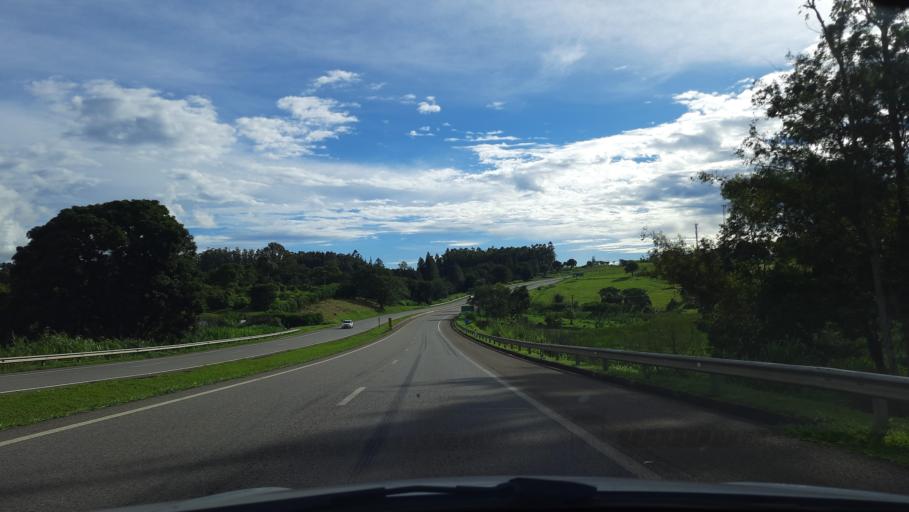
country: BR
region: Sao Paulo
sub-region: Sao Joao Da Boa Vista
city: Sao Joao da Boa Vista
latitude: -21.9684
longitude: -46.7406
